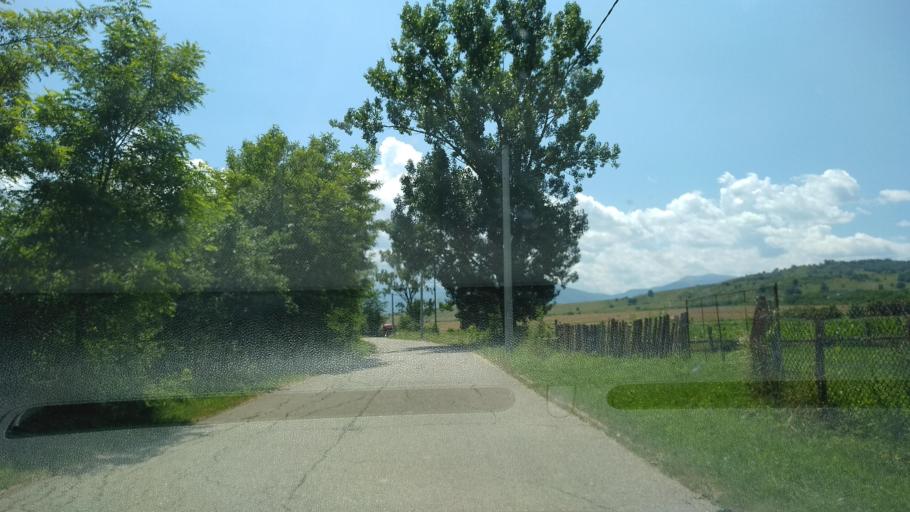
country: RO
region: Hunedoara
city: Densus
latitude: 45.5766
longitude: 22.8083
